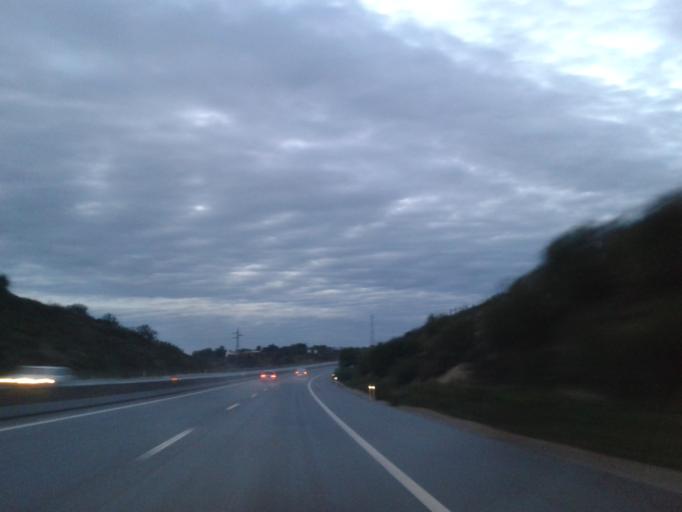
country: PT
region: Faro
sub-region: Lagoa
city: Estombar
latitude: 37.1568
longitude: -8.4814
